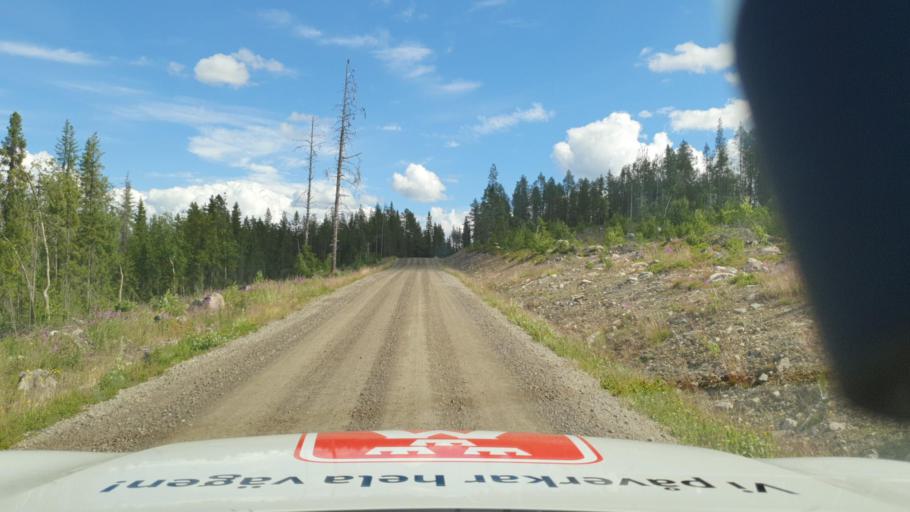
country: SE
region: Vaesterbotten
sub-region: Sorsele Kommun
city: Sorsele
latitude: 65.6693
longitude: 17.3019
